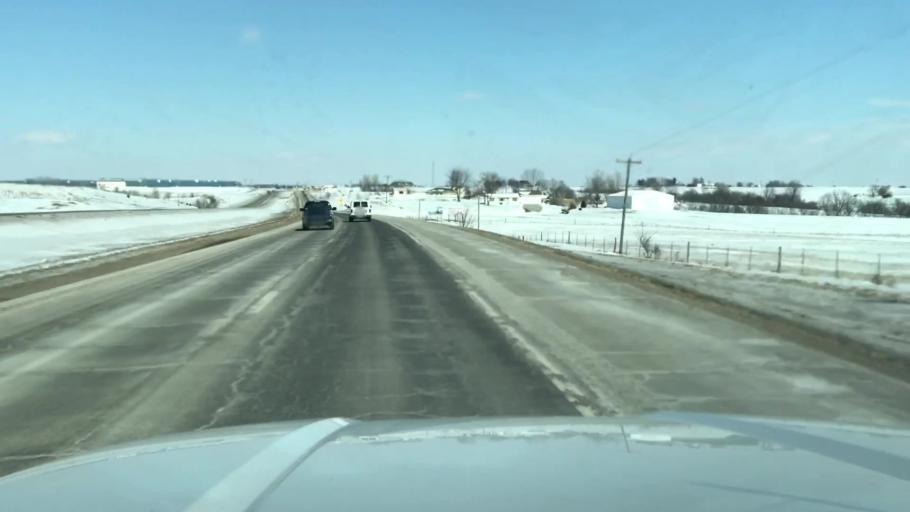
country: US
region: Missouri
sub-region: Nodaway County
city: Maryville
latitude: 40.3001
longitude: -94.8747
